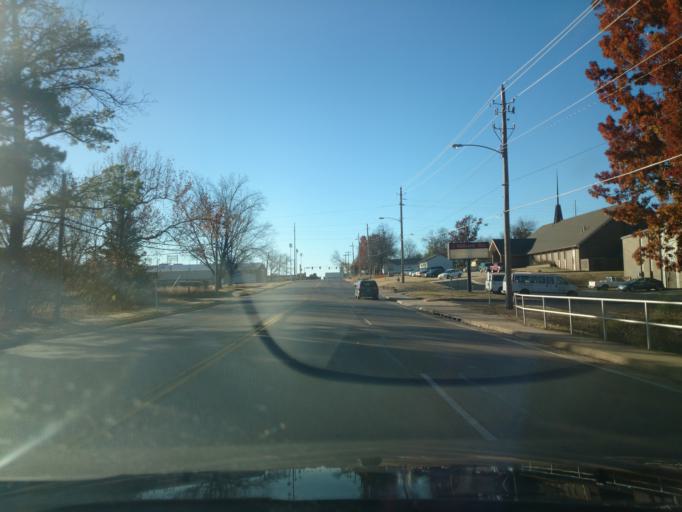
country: US
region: Oklahoma
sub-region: Payne County
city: Stillwater
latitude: 36.1328
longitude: -97.0695
